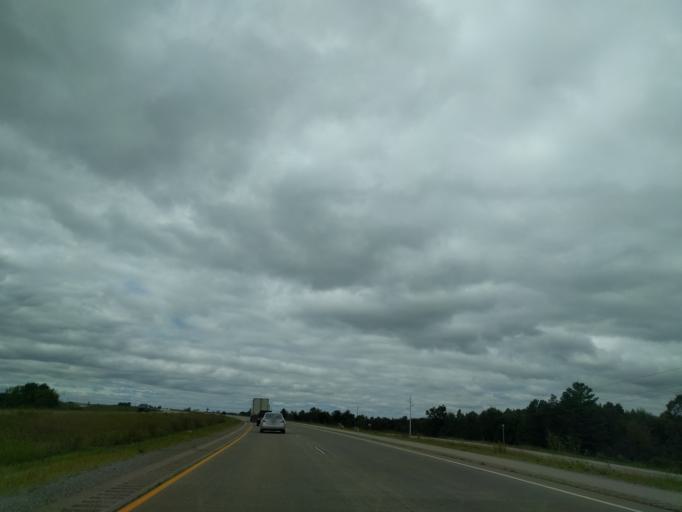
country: US
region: Wisconsin
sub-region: Marinette County
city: Peshtigo
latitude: 45.0615
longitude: -87.7076
